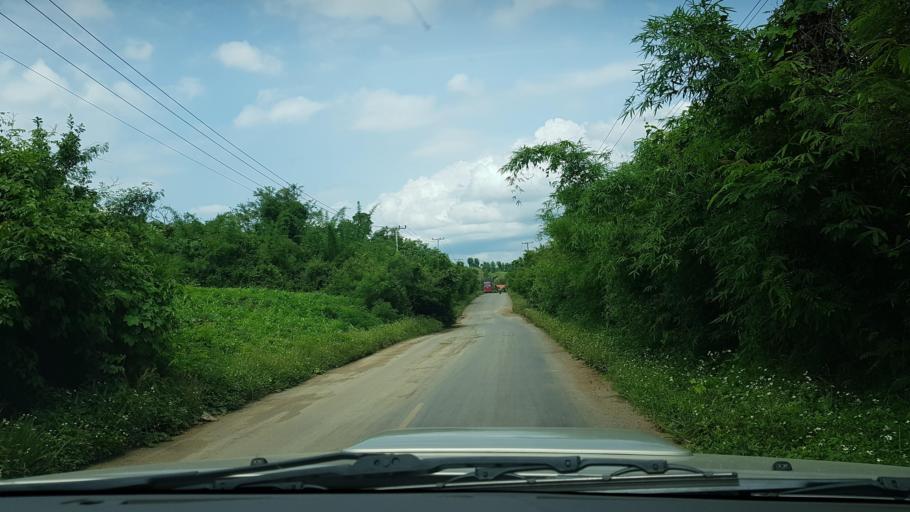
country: TH
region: Nan
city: Chaloem Phra Kiat
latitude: 20.0219
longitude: 101.3265
